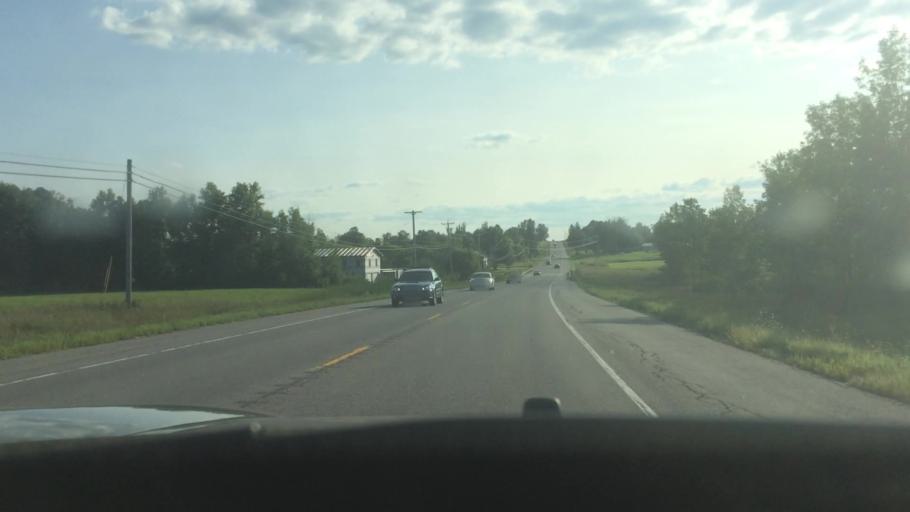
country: US
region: New York
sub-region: St. Lawrence County
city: Canton
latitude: 44.6277
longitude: -75.0903
